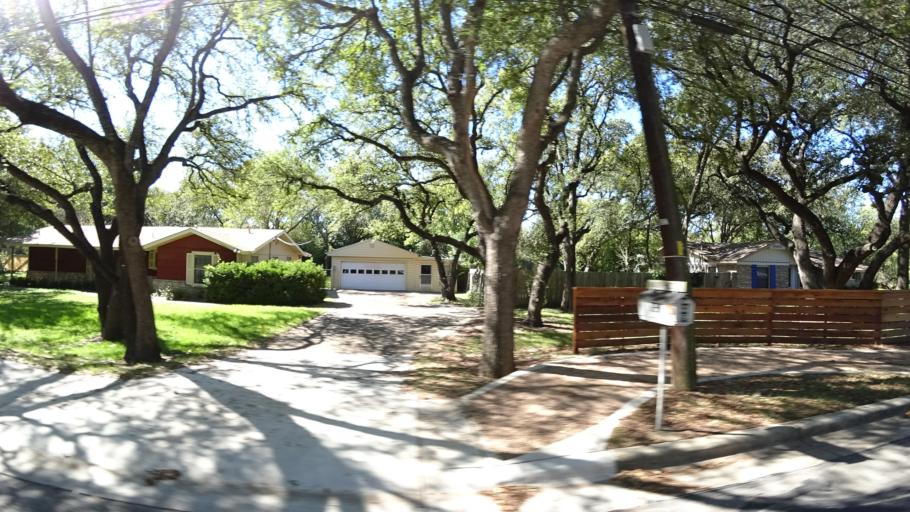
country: US
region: Texas
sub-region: Travis County
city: Rollingwood
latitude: 30.2266
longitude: -97.8060
